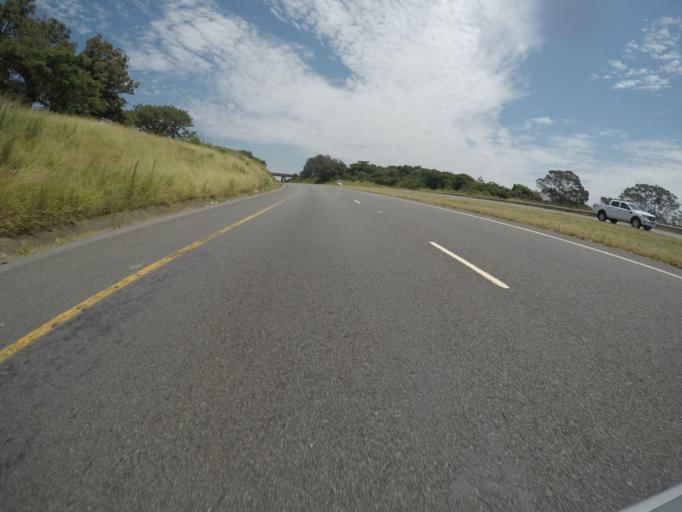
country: ZA
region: Eastern Cape
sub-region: Buffalo City Metropolitan Municipality
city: East London
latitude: -32.9678
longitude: 27.8773
